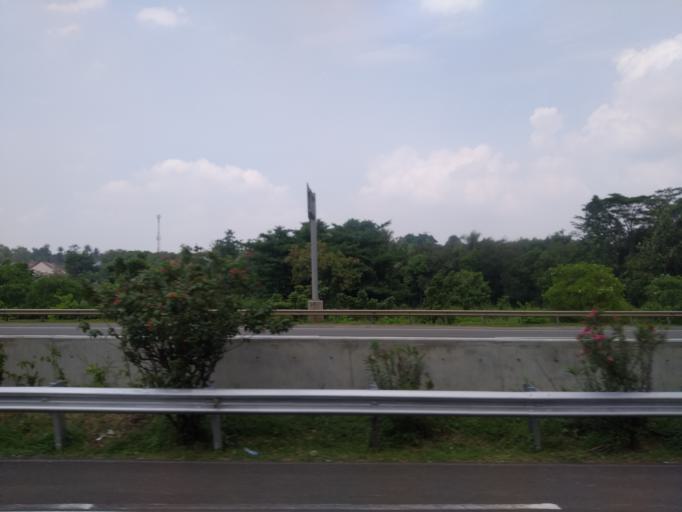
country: ID
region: West Java
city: Citeureup
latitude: -6.4709
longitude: 106.8800
